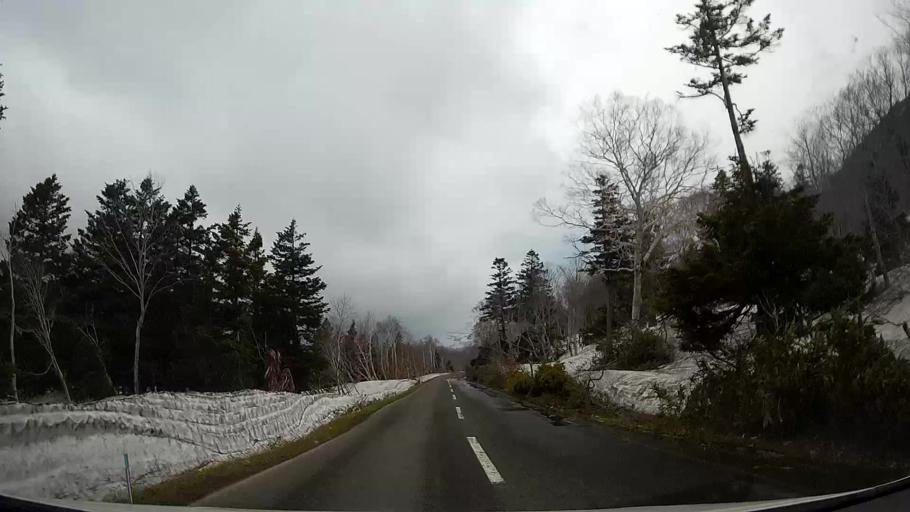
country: JP
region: Aomori
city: Aomori Shi
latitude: 40.6350
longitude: 140.8792
